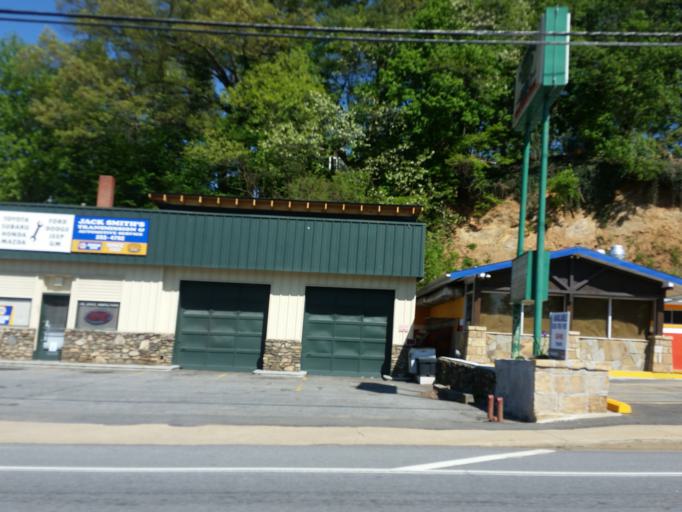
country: US
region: North Carolina
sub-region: Buncombe County
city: Asheville
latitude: 35.5868
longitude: -82.5517
